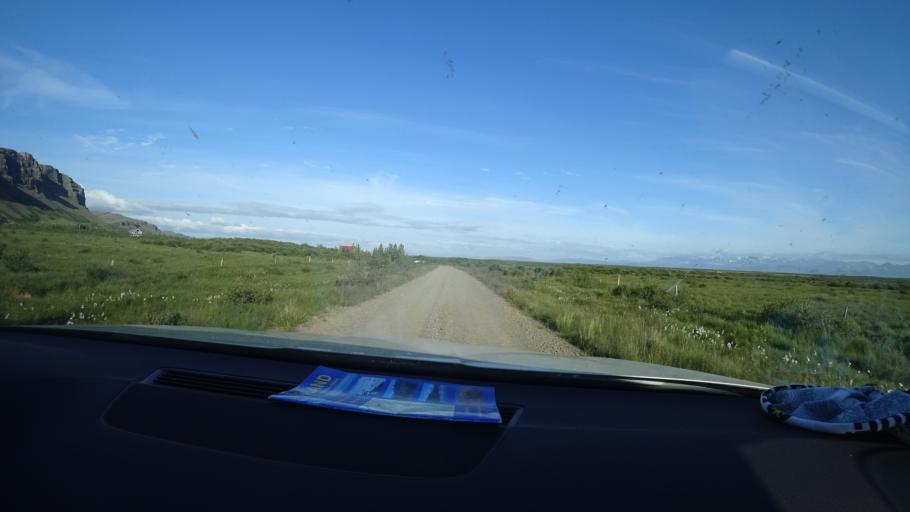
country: IS
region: West
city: Borgarnes
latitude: 64.6915
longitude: -21.9393
